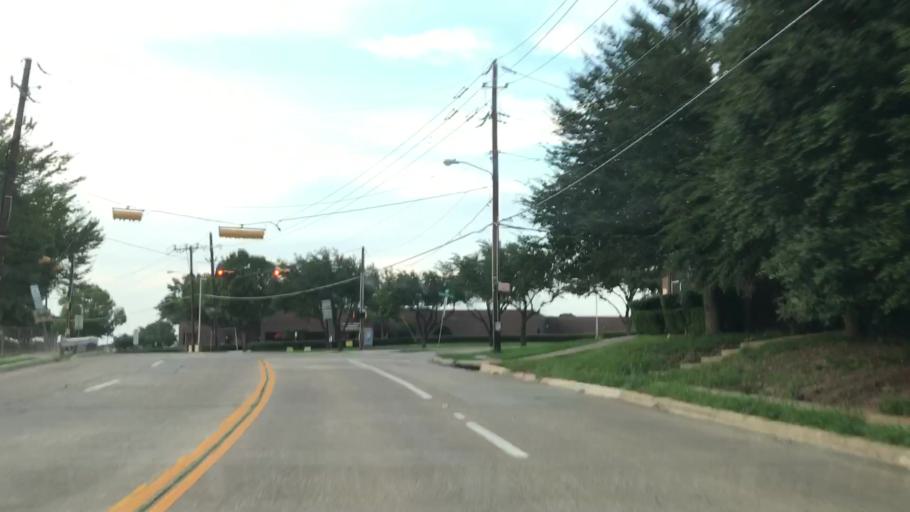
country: US
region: Texas
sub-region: Dallas County
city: Addison
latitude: 32.9999
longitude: -96.8640
